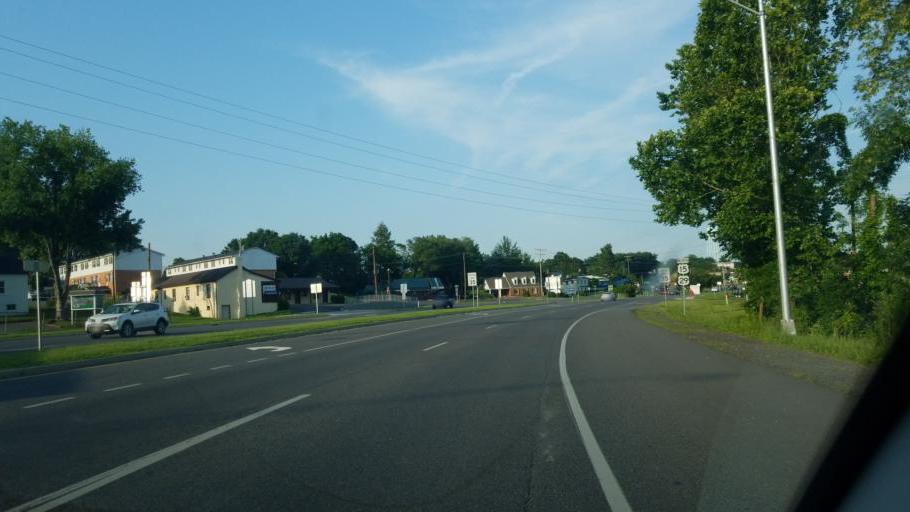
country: US
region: Virginia
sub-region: Culpeper County
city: Culpeper
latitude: 38.4804
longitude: -77.9922
